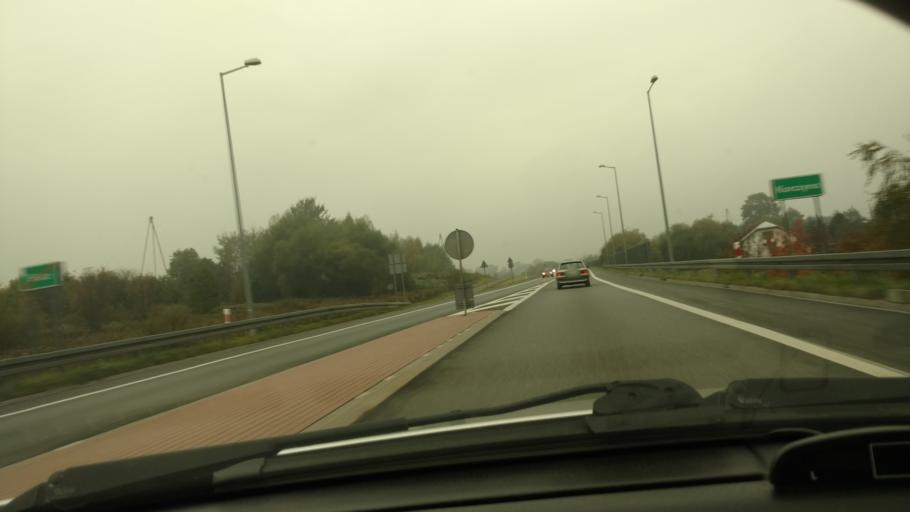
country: PL
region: Lesser Poland Voivodeship
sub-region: Powiat gorlicki
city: Biecz
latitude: 49.7234
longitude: 21.2576
